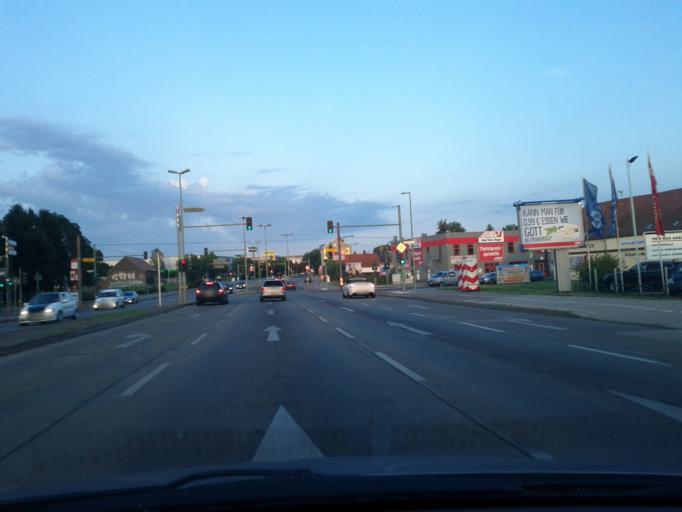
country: DE
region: Berlin
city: Mahlsdorf
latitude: 52.5048
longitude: 13.6125
